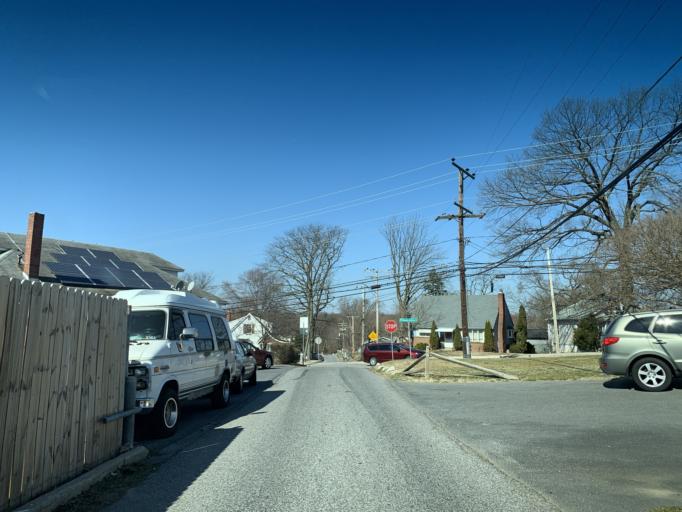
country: US
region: Maryland
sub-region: Baltimore County
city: Rosedale
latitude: 39.3292
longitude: -76.5016
